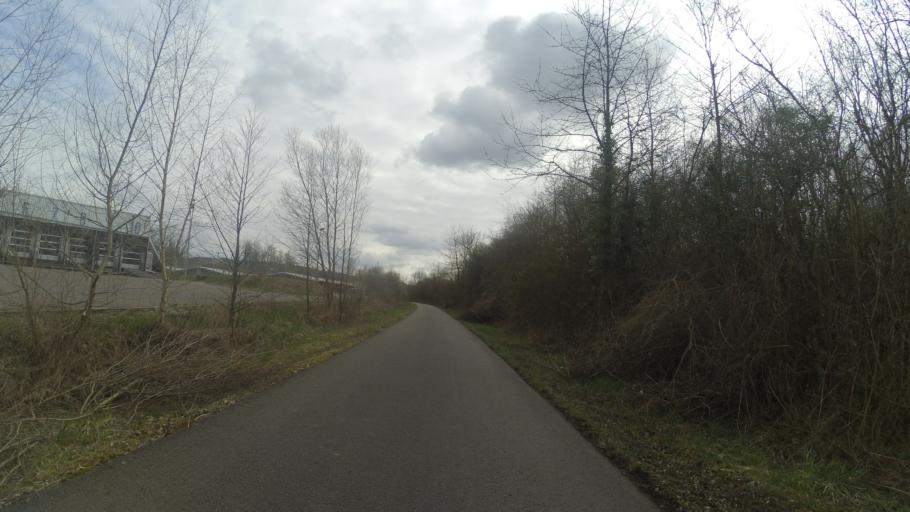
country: DE
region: Saarland
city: Gersheim
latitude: 49.1544
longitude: 7.2077
